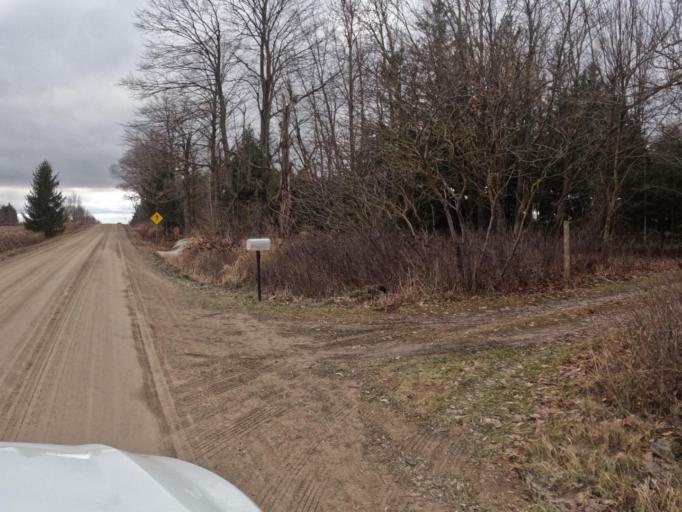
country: CA
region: Ontario
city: Shelburne
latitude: 43.8748
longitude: -80.3797
